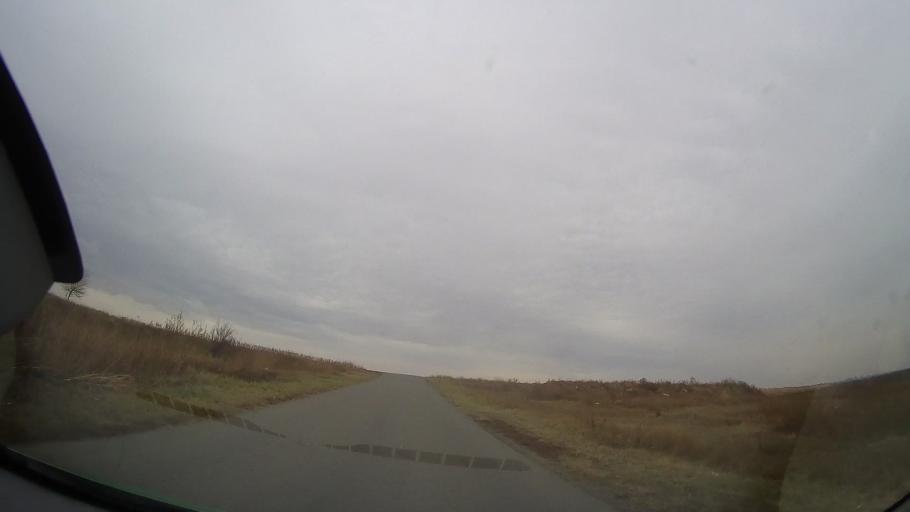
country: RO
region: Prahova
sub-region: Comuna Ceptura
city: Ceptura de Jos
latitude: 45.0123
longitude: 26.3482
